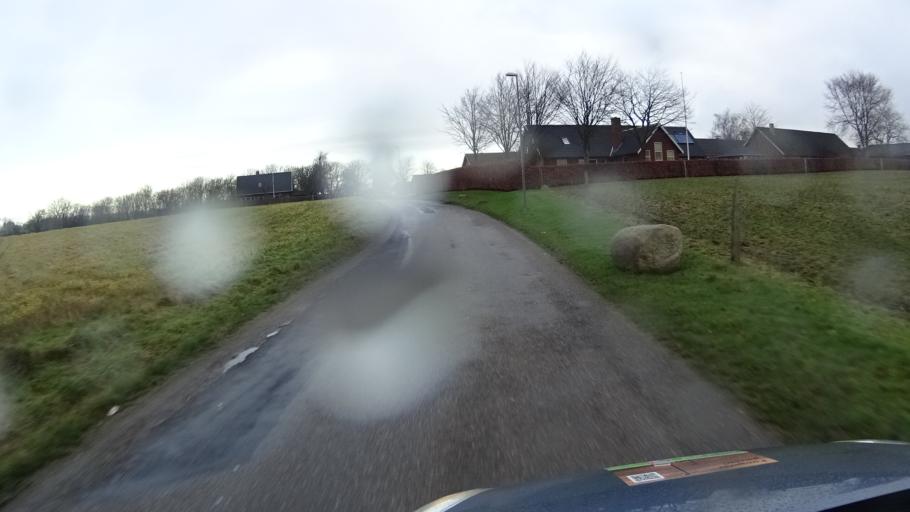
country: DK
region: South Denmark
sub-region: Vejle Kommune
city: Vejle
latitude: 55.7413
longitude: 9.5054
